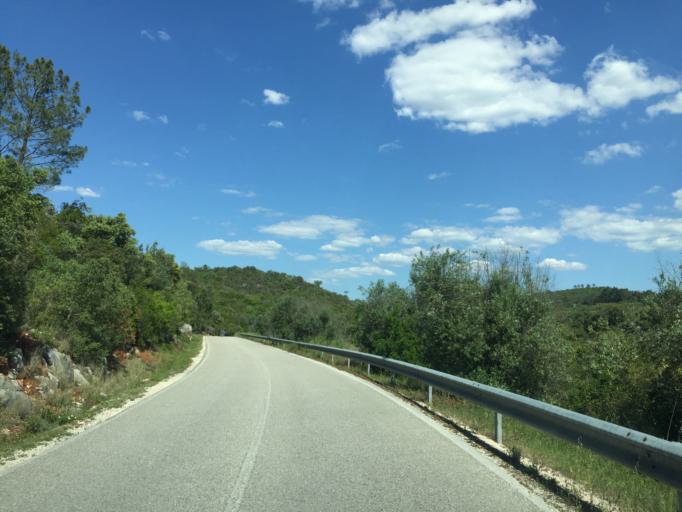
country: PT
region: Leiria
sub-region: Alvaiazere
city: Alvaiazere
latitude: 39.8034
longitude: -8.4158
